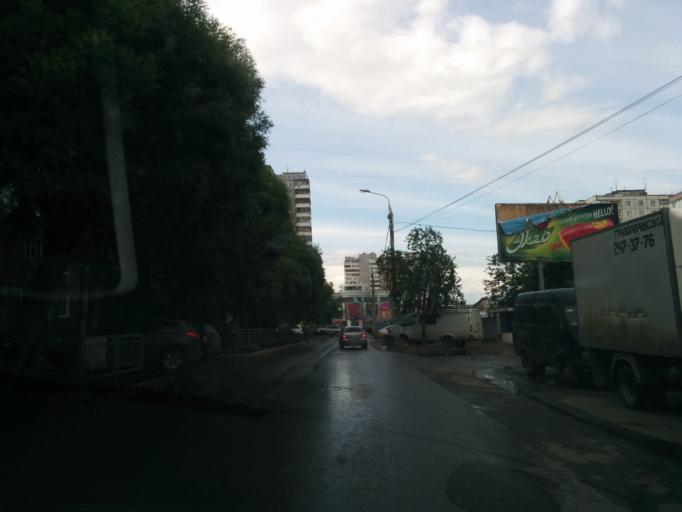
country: RU
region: Perm
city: Kondratovo
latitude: 57.9963
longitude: 56.1560
